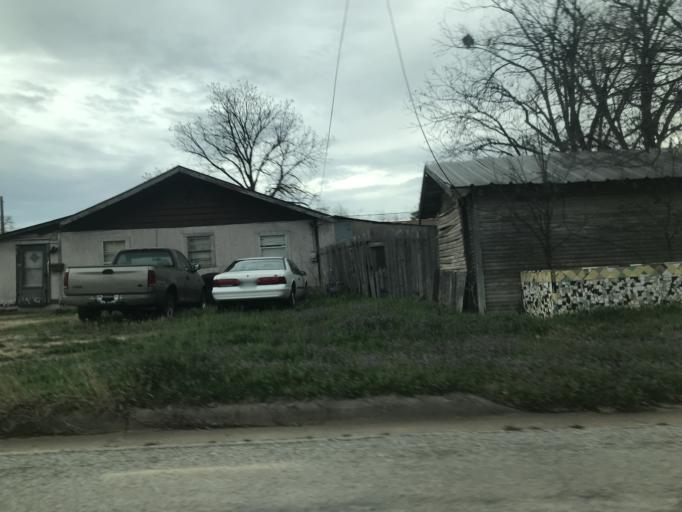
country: US
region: Texas
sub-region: Taylor County
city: Abilene
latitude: 32.4669
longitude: -99.7446
